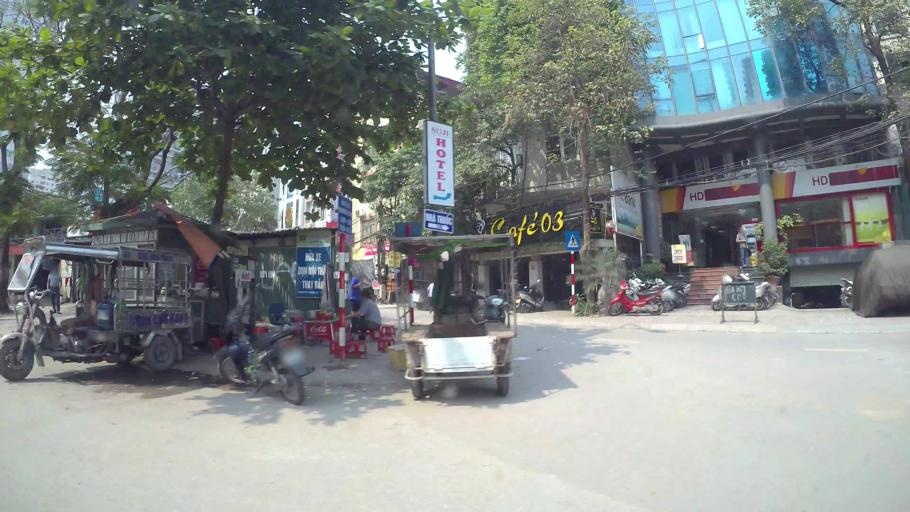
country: VN
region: Ha Noi
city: Thanh Xuan
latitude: 21.0040
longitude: 105.8069
